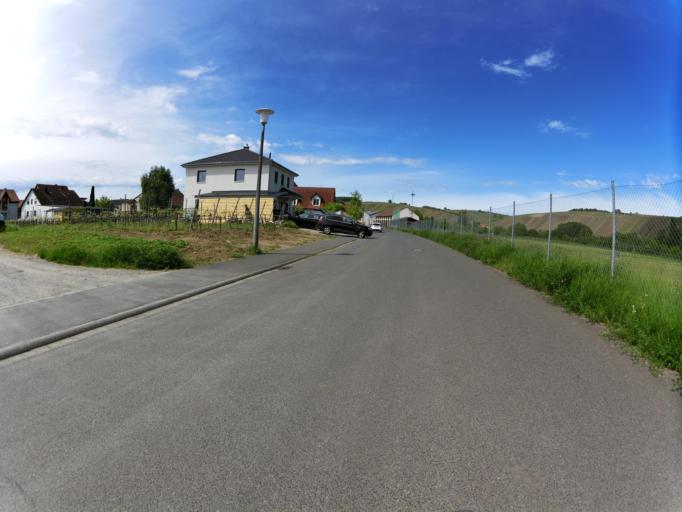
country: DE
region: Bavaria
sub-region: Regierungsbezirk Unterfranken
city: Nordheim
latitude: 49.8613
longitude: 10.1884
